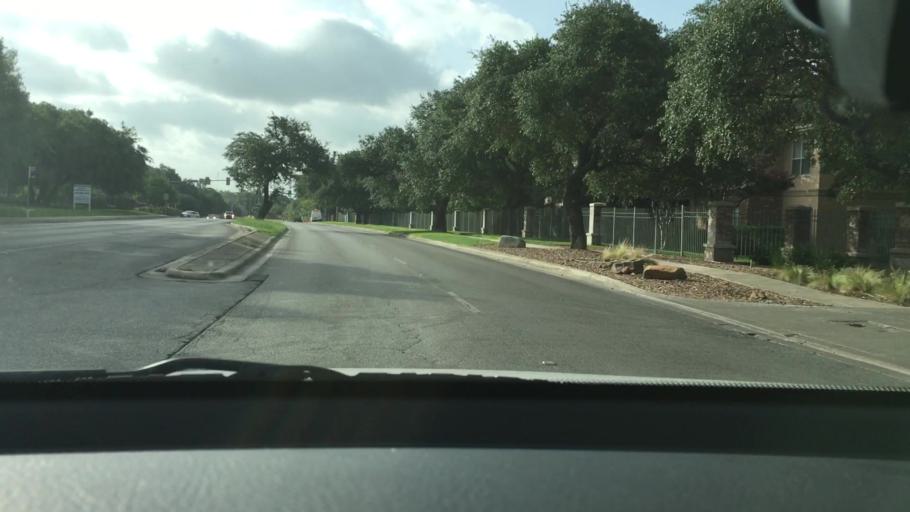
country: US
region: Texas
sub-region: Bexar County
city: Hollywood Park
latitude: 29.6029
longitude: -98.4610
